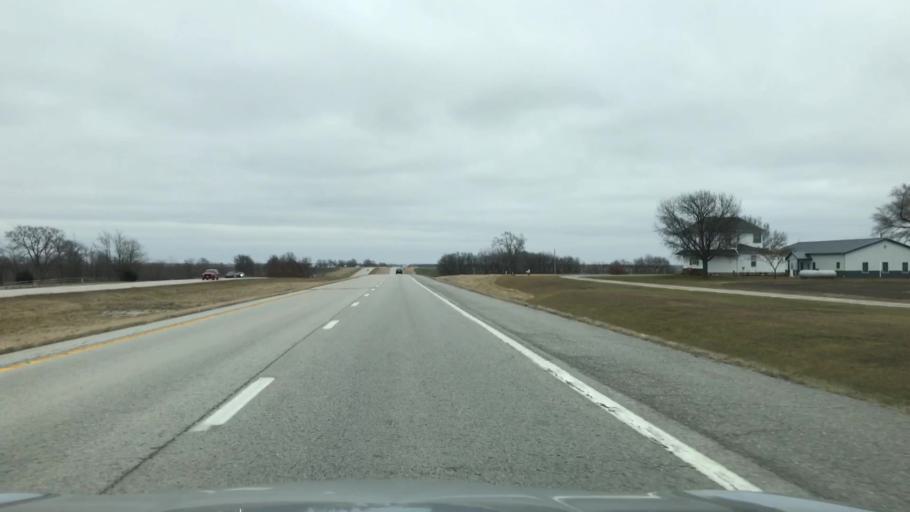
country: US
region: Missouri
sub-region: Livingston County
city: Chillicothe
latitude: 39.7760
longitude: -93.4889
